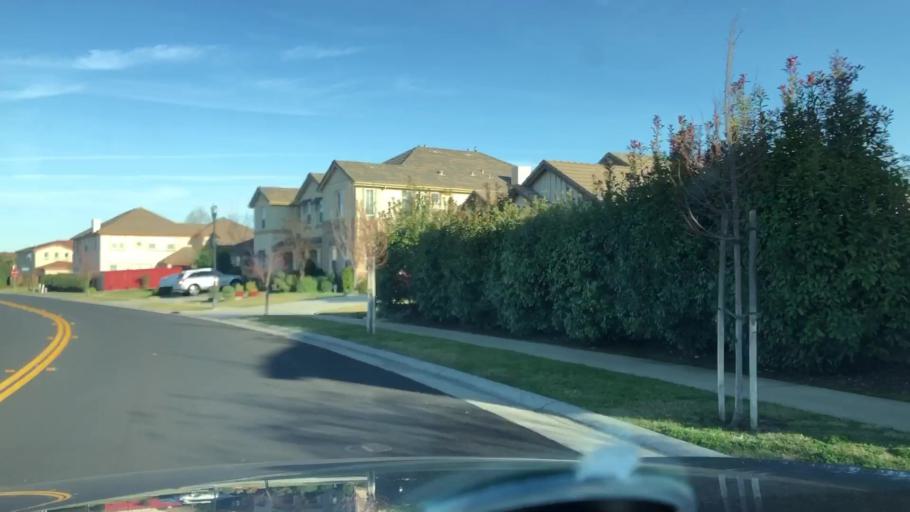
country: US
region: California
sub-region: Sacramento County
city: Laguna
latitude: 38.3985
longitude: -121.4060
